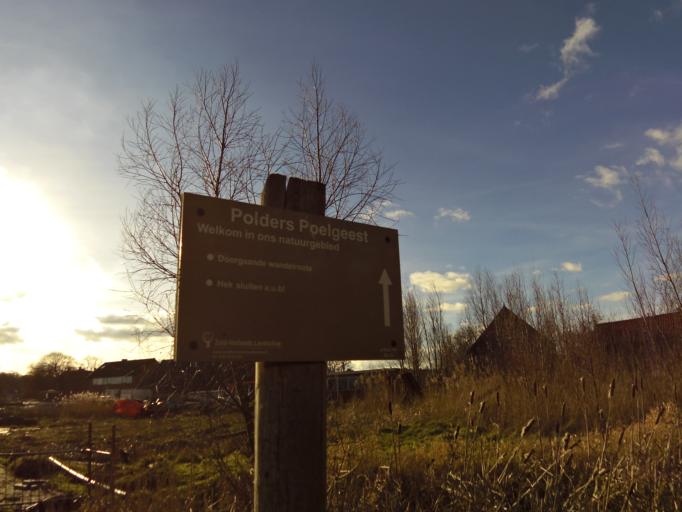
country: NL
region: South Holland
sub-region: Gemeente Oegstgeest
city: Oegstgeest
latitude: 52.1835
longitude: 4.4920
